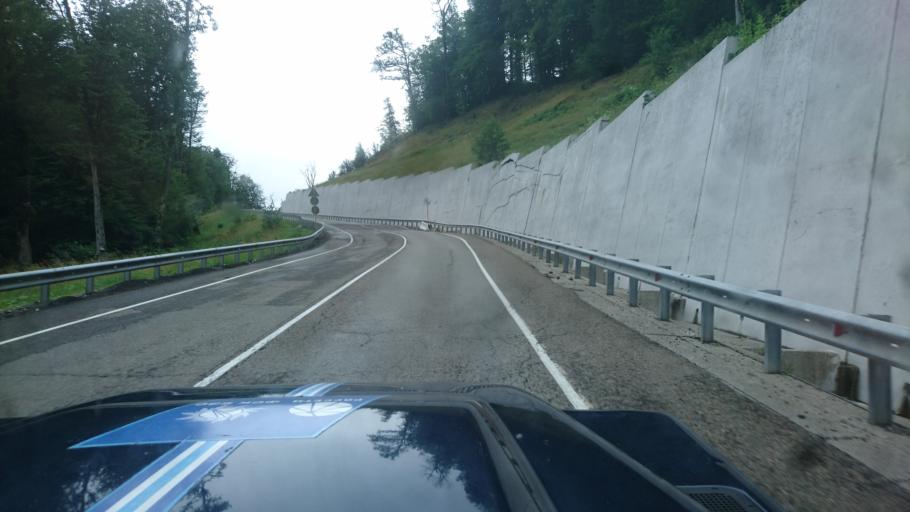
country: RU
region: Krasnodarskiy
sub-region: Sochi City
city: Krasnaya Polyana
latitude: 43.6612
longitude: 40.3108
